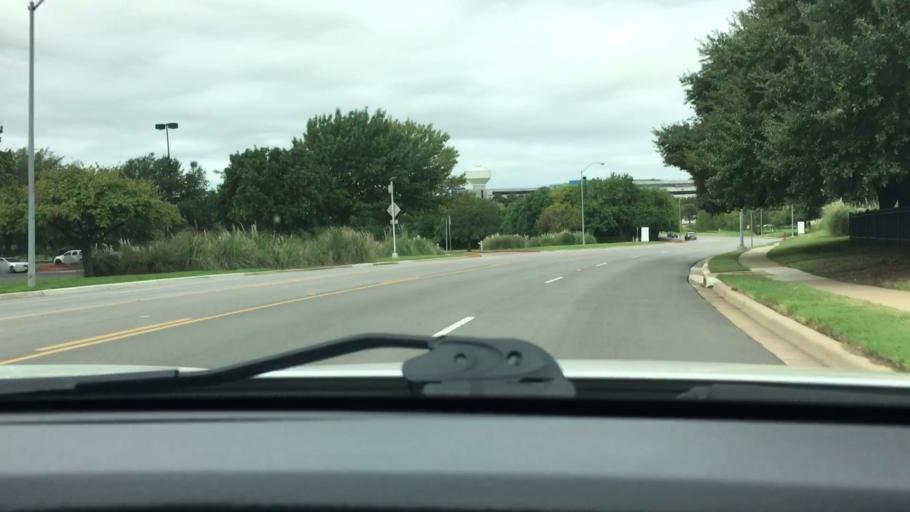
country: US
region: Texas
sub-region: Williamson County
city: Round Rock
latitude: 30.4858
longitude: -97.6652
